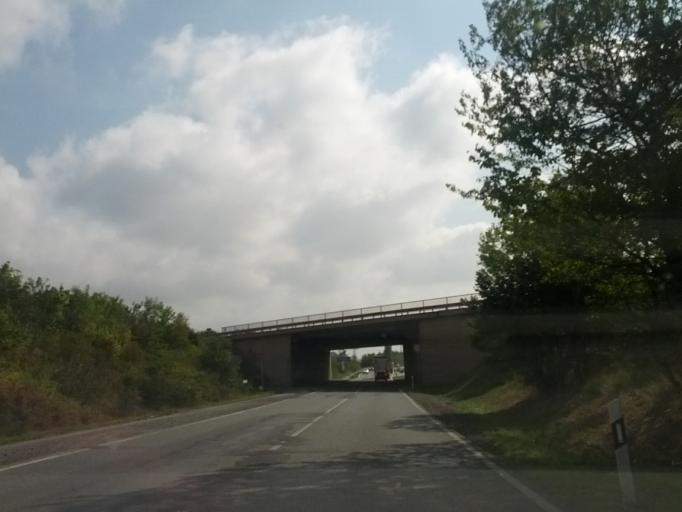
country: DE
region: Thuringia
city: Neudietendorf
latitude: 50.8934
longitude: 10.9321
